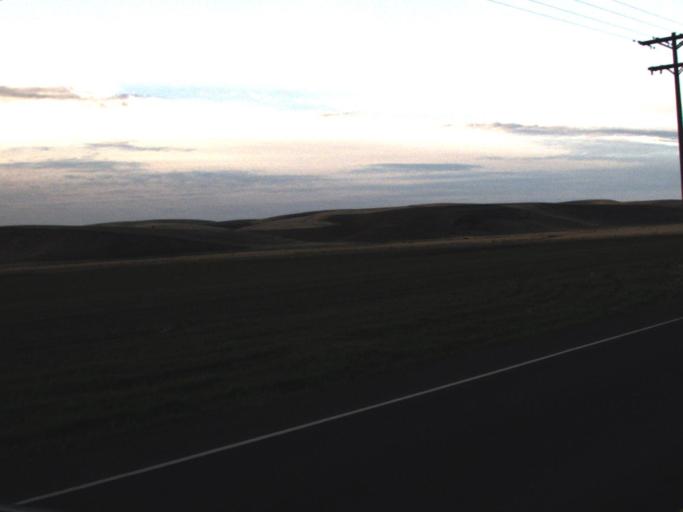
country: US
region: Washington
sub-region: Whitman County
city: Colfax
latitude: 46.8062
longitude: -117.6594
